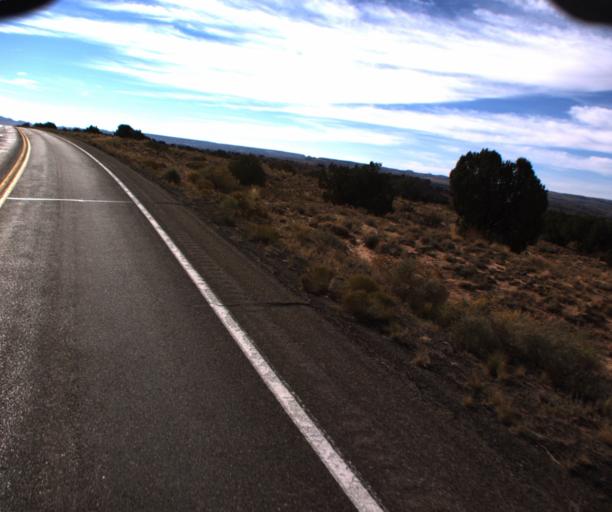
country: US
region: Arizona
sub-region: Coconino County
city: Kaibito
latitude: 36.6704
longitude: -111.2562
